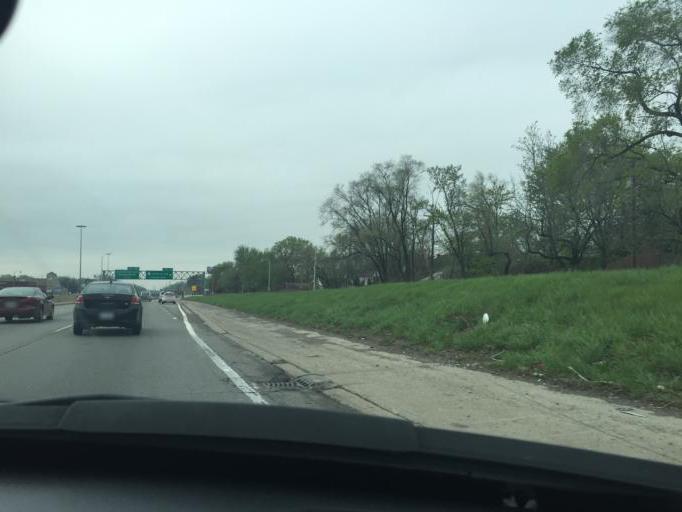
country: US
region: Michigan
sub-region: Oakland County
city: Oak Park
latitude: 42.4055
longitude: -83.2186
